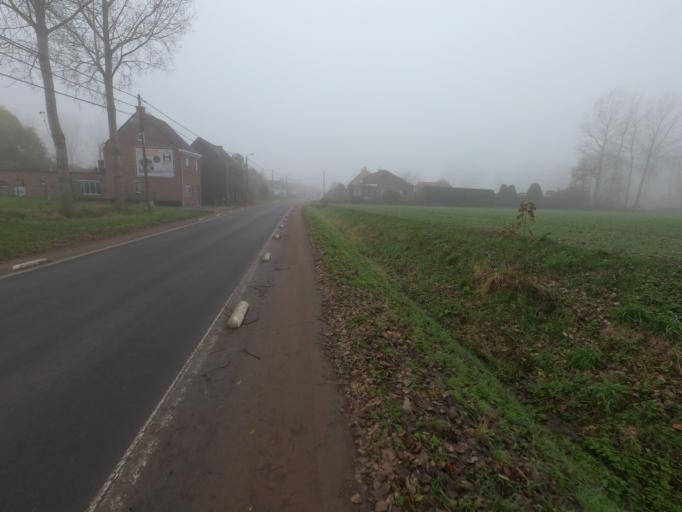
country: BE
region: Flanders
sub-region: Provincie Oost-Vlaanderen
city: Kruibeke
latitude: 51.1731
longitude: 4.2859
